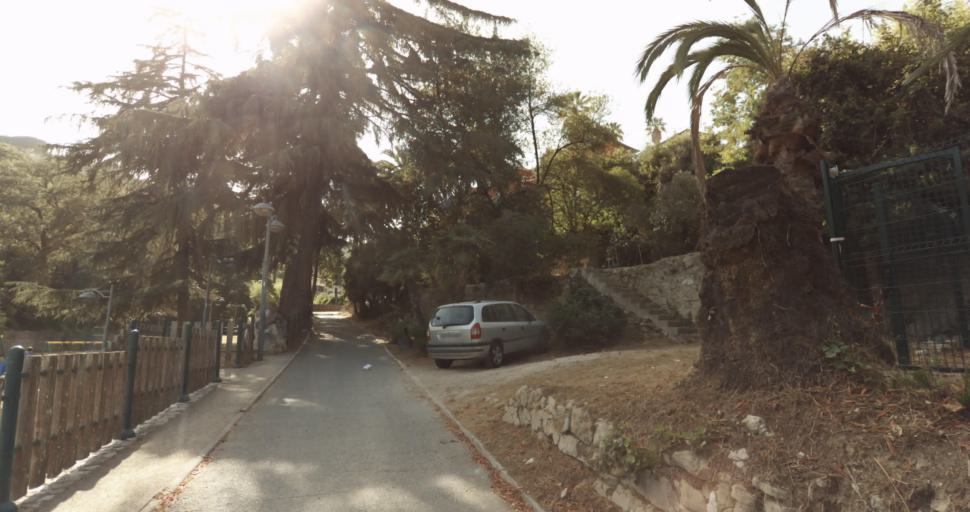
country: FR
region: Provence-Alpes-Cote d'Azur
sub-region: Departement des Alpes-Maritimes
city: Roquebrune-Cap-Martin
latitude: 43.7745
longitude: 7.4873
